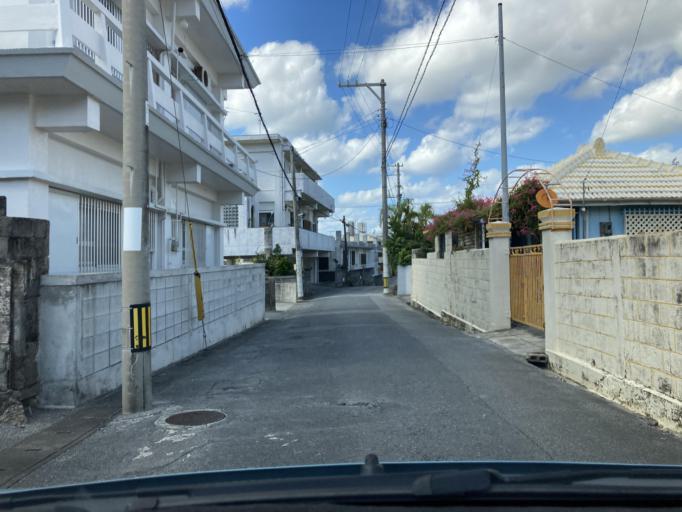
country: JP
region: Okinawa
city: Okinawa
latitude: 26.3271
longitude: 127.7925
